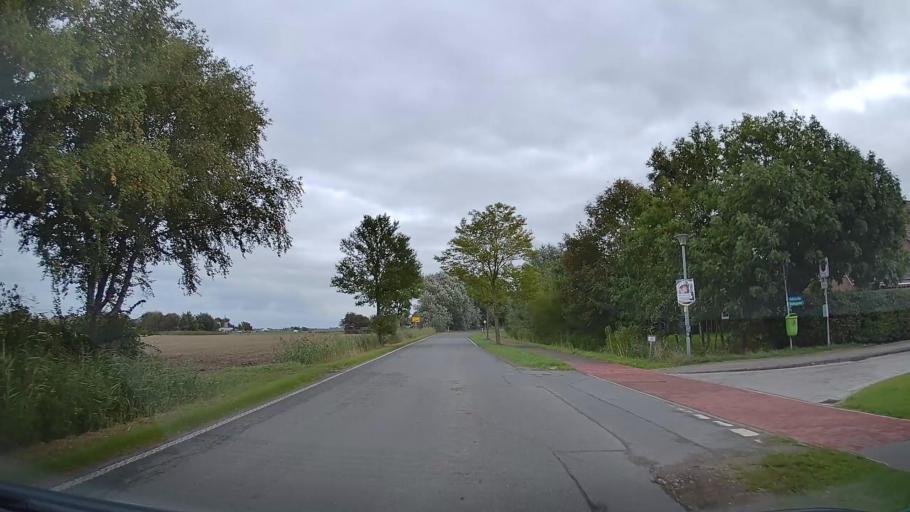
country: DE
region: Schleswig-Holstein
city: Klanxbull
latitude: 54.8669
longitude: 8.6739
